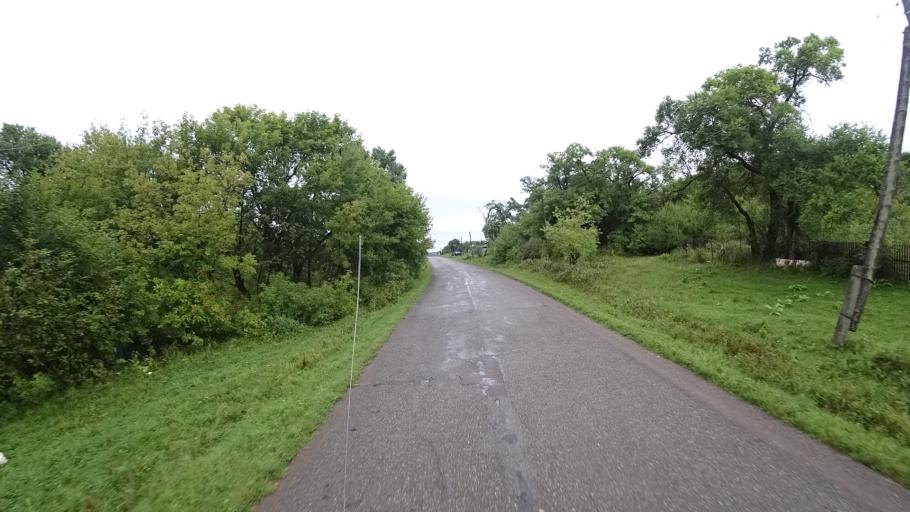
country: RU
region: Primorskiy
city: Monastyrishche
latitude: 44.2682
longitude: 132.4203
